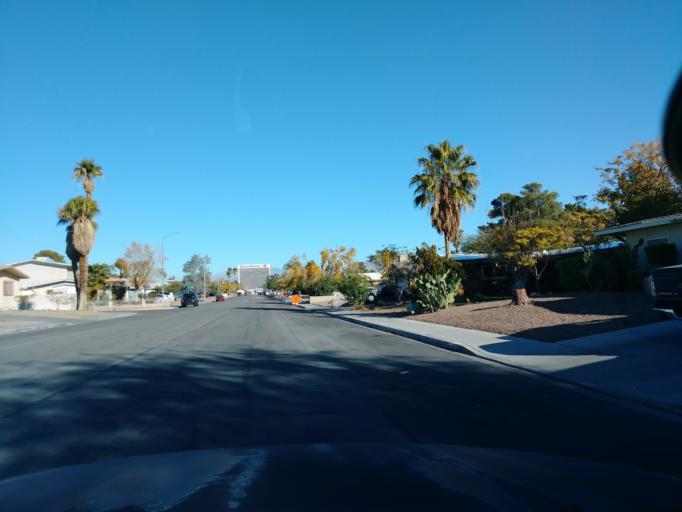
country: US
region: Nevada
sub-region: Clark County
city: Spring Valley
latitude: 36.1675
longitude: -115.2469
